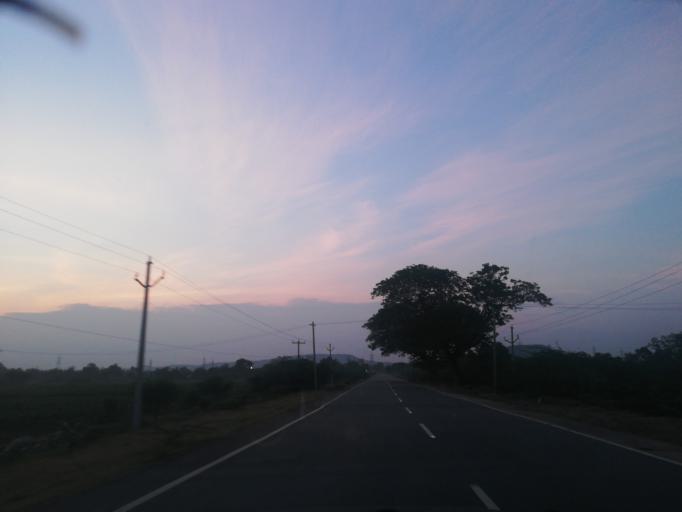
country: IN
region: Andhra Pradesh
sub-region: Guntur
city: Macherla
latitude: 16.6795
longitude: 79.2621
